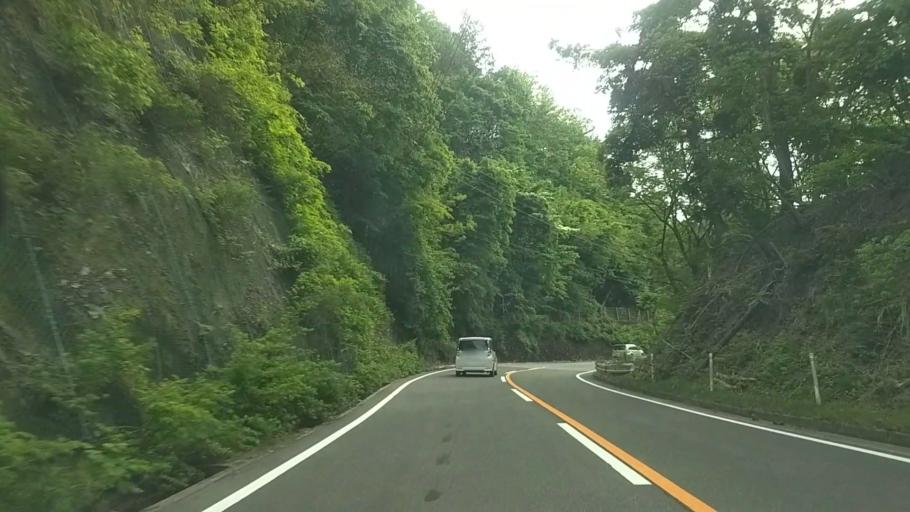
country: JP
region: Yamanashi
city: Fujikawaguchiko
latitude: 35.5211
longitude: 138.6194
